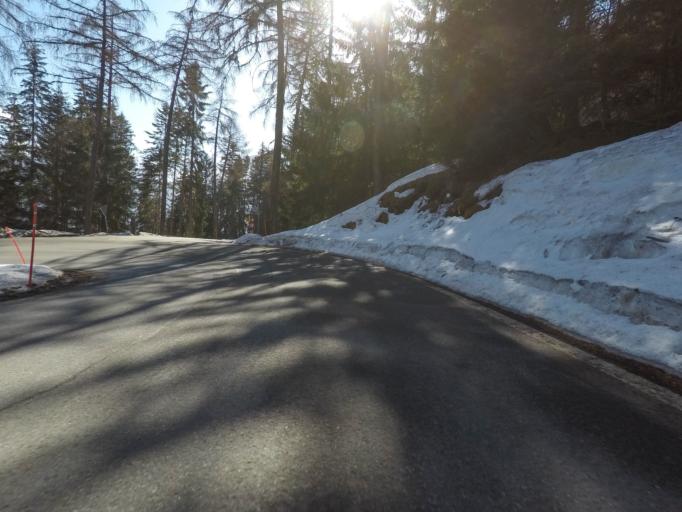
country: CH
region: Valais
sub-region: Herens District
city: Vex
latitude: 46.1942
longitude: 7.3851
